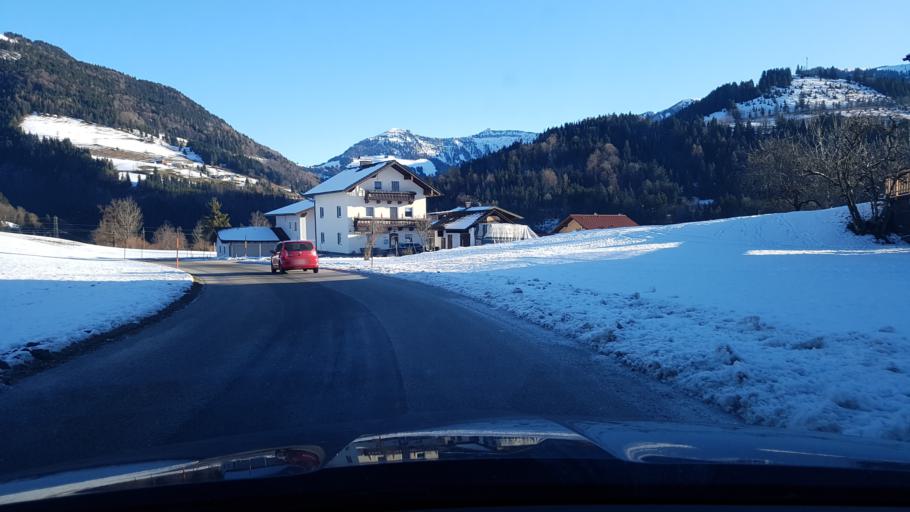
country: AT
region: Salzburg
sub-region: Politischer Bezirk Hallein
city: Scheffau am Tennengebirge
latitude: 47.6509
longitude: 13.2123
